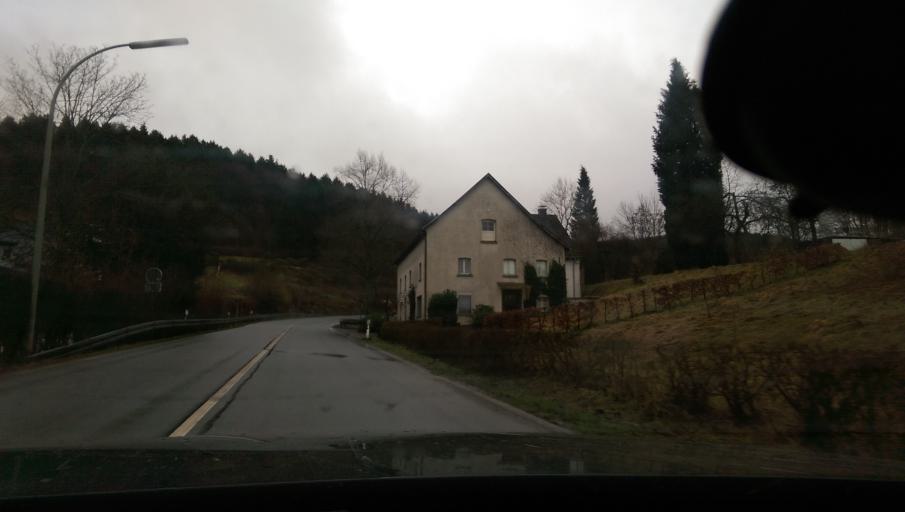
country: DE
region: North Rhine-Westphalia
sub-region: Regierungsbezirk Arnsberg
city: Sundern
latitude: 51.2566
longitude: 7.9681
